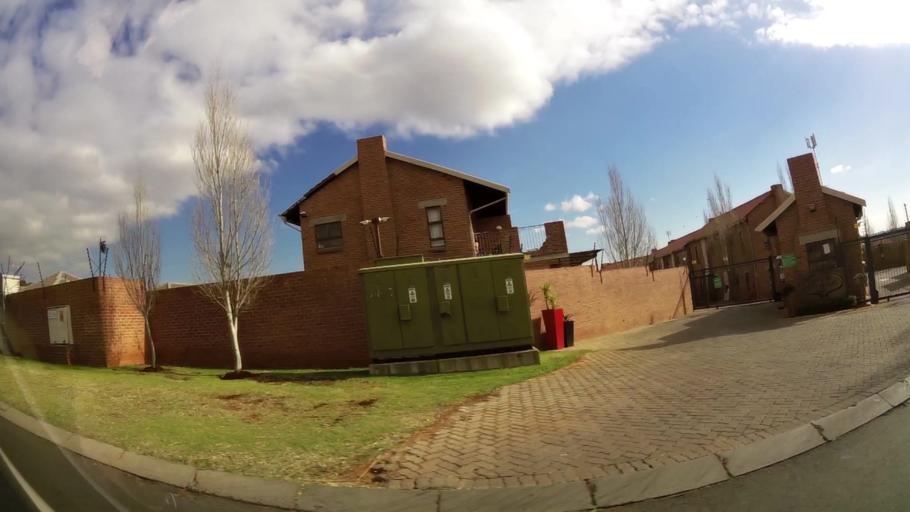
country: ZA
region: Gauteng
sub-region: City of Johannesburg Metropolitan Municipality
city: Roodepoort
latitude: -26.0964
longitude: 27.8728
